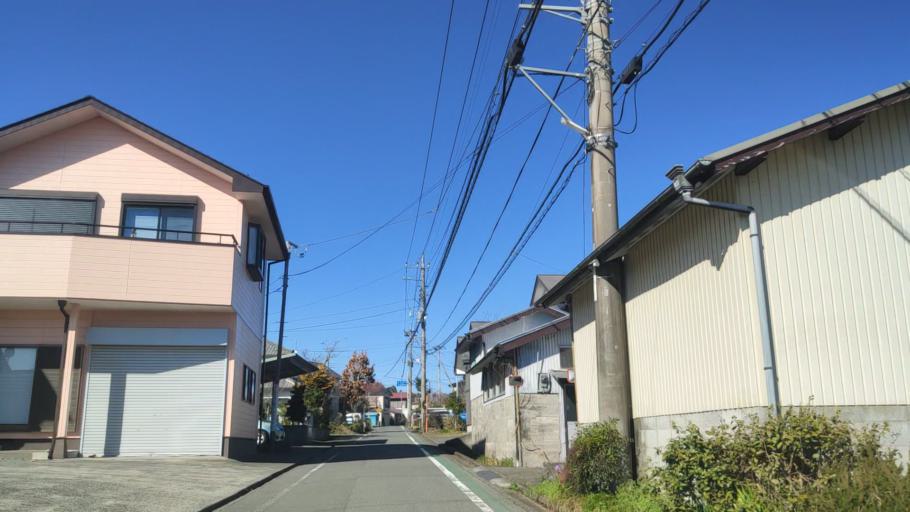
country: JP
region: Shizuoka
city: Fujinomiya
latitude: 35.3098
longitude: 138.5758
